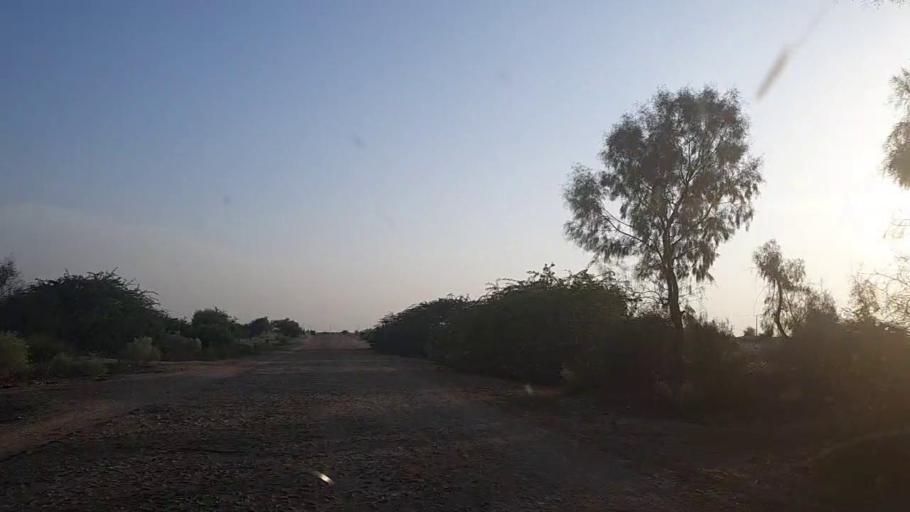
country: PK
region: Sindh
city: Khanpur
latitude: 27.6470
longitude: 69.4612
